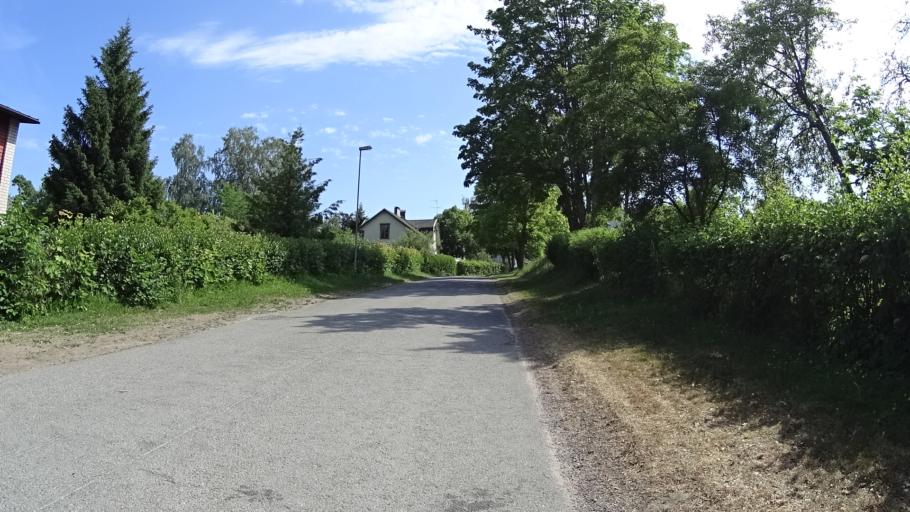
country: FI
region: Uusimaa
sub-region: Raaseporin
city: Karis
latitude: 60.0734
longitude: 23.6686
